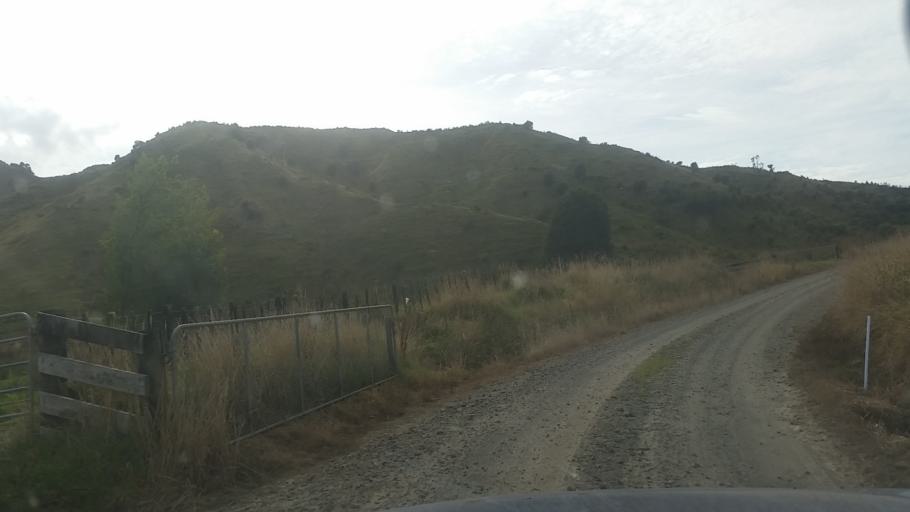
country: NZ
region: Taranaki
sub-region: New Plymouth District
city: Waitara
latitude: -39.1278
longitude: 174.6965
